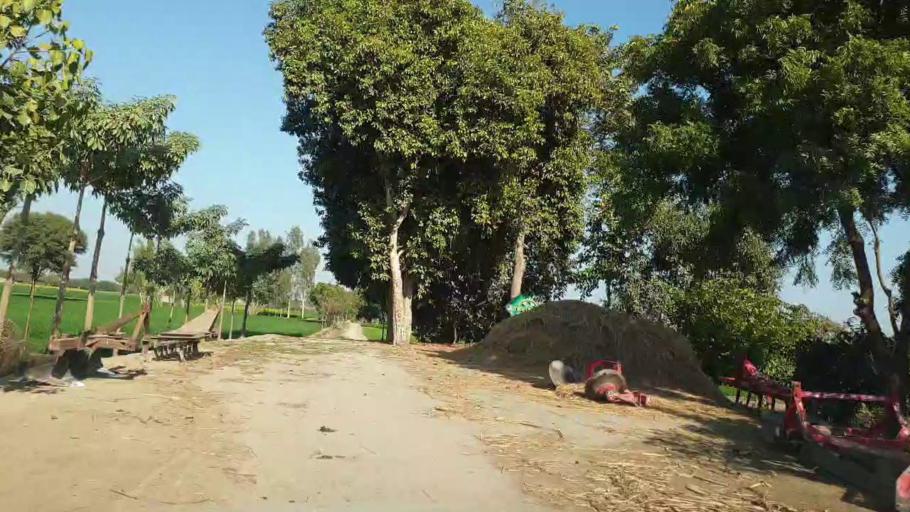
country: PK
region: Sindh
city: Tando Allahyar
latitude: 25.4880
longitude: 68.6565
